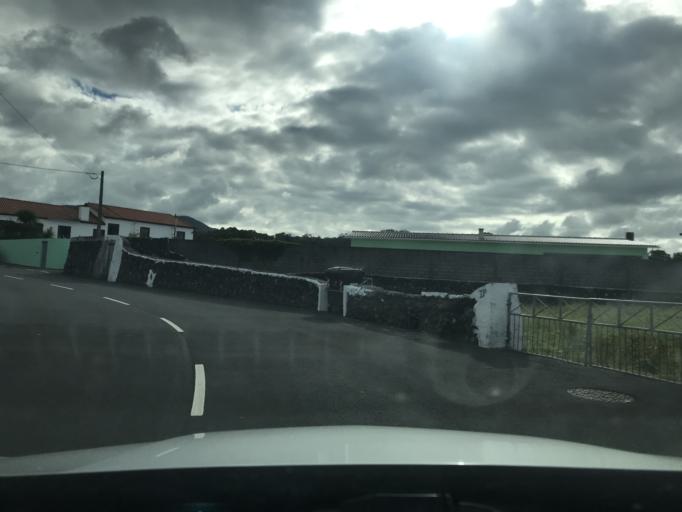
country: PT
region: Azores
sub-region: Angra do Heroismo
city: Angra do Heroismo
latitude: 38.6667
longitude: -27.2526
